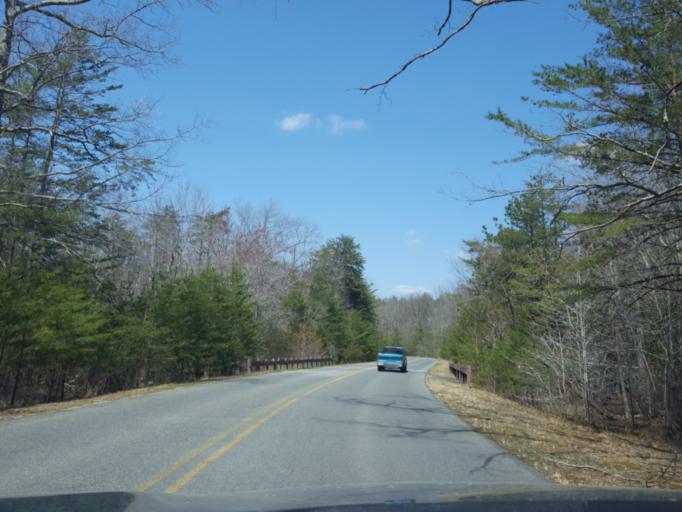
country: US
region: Maryland
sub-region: Prince George's County
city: Brandywine
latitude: 38.6537
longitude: -76.8333
